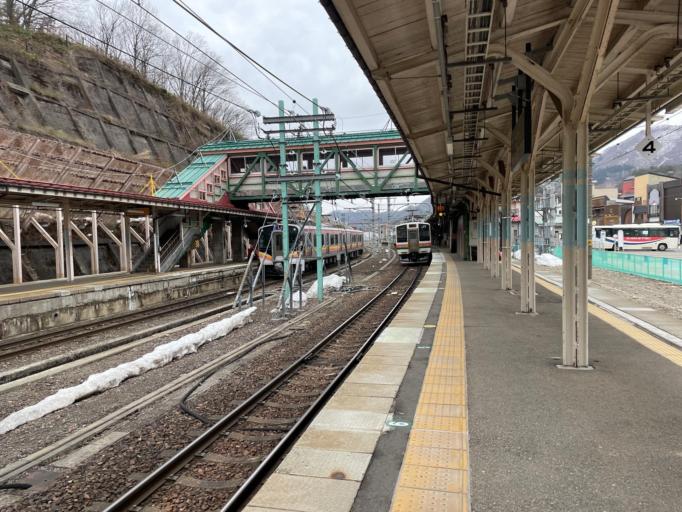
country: JP
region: Gunma
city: Numata
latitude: 36.7796
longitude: 138.9690
